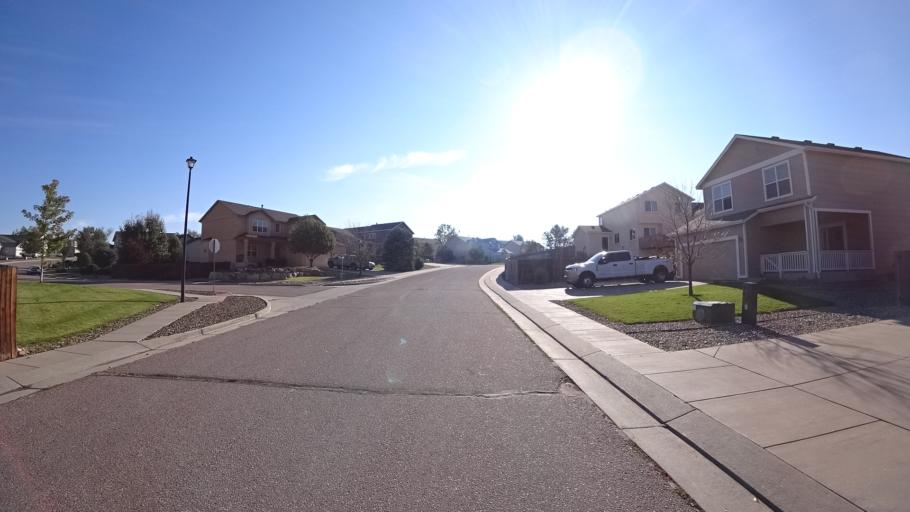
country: US
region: Colorado
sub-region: El Paso County
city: Cimarron Hills
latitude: 38.8913
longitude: -104.6906
